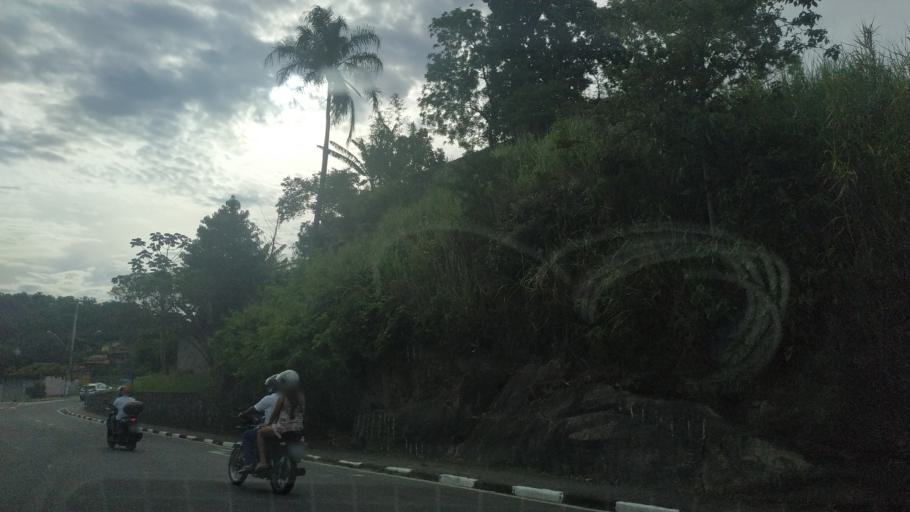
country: BR
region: Sao Paulo
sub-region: Ilhabela
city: Ilhabela
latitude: -23.8218
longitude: -45.3769
